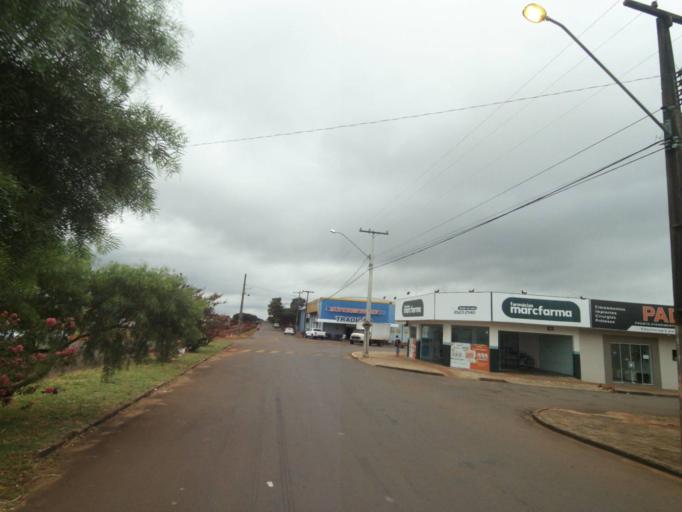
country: BR
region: Parana
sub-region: Campo Mourao
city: Campo Mourao
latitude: -24.0126
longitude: -52.3557
